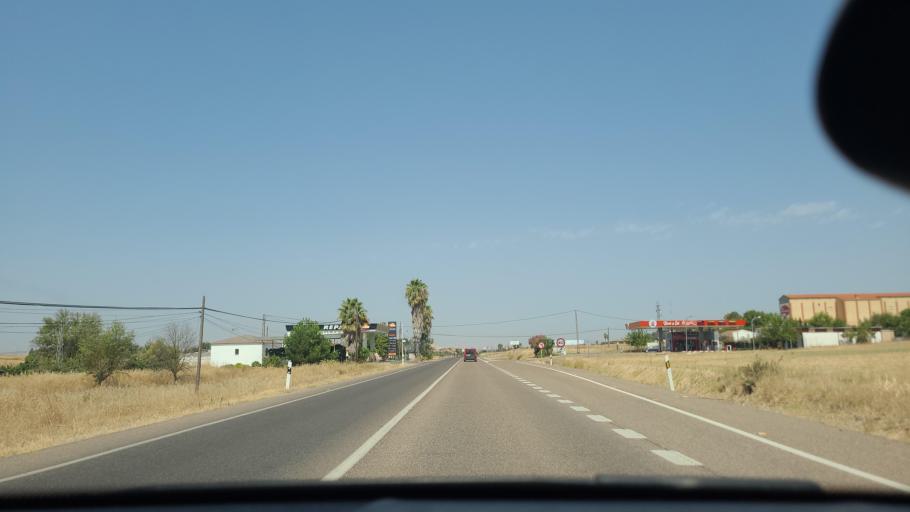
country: ES
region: Extremadura
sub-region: Provincia de Badajoz
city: Badajoz
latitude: 38.8479
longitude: -6.9373
